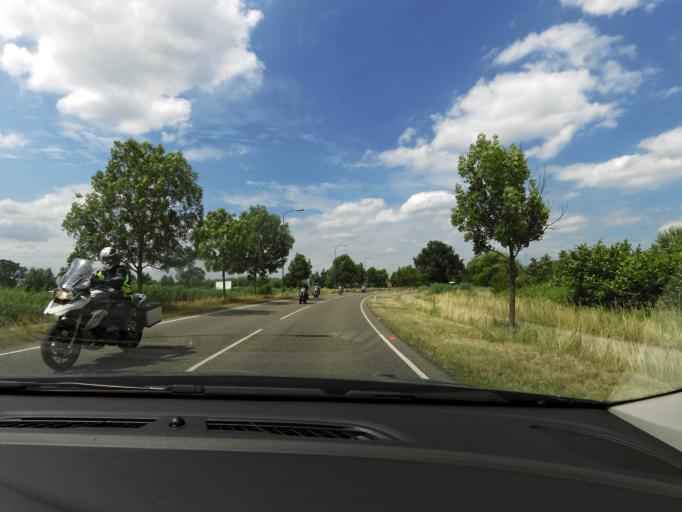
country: NL
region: North Brabant
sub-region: Gemeente Baarle-Nassau
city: Baarle-Nassau
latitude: 51.4976
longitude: 4.8717
